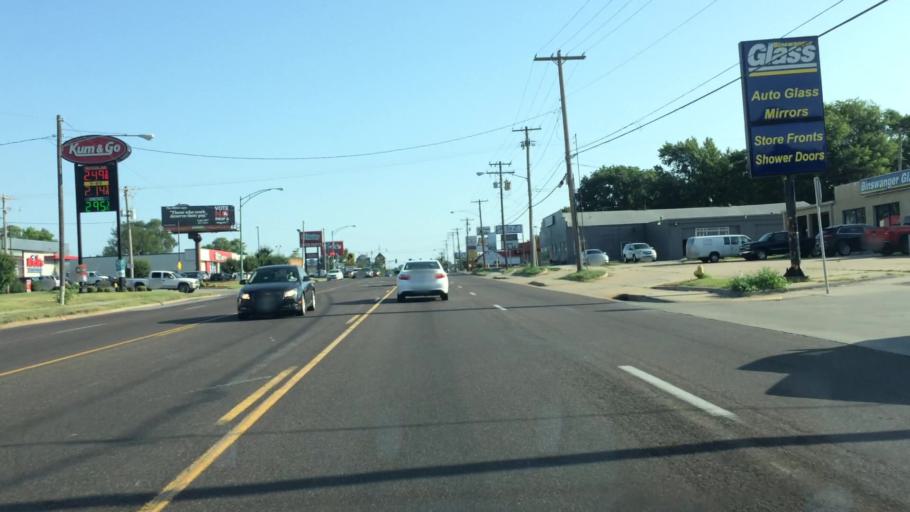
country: US
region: Missouri
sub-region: Greene County
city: Springfield
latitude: 37.1749
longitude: -93.2953
